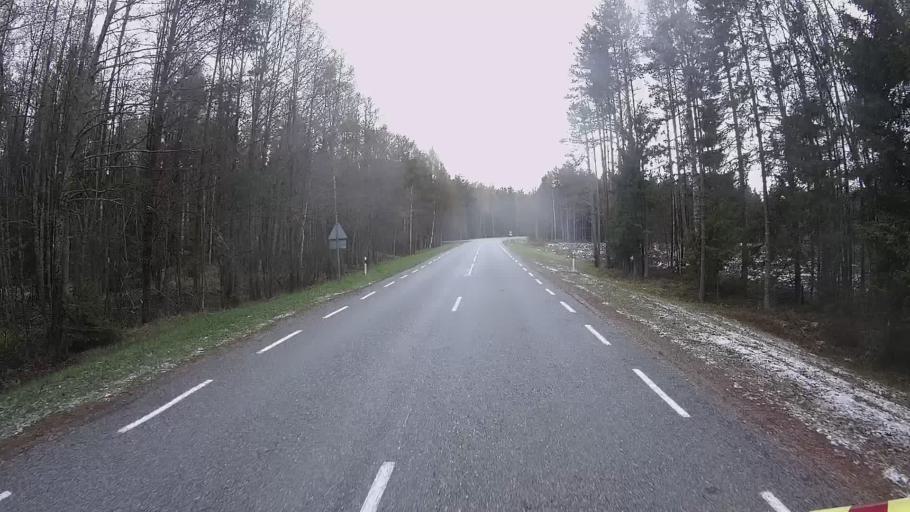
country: EE
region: Hiiumaa
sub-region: Kaerdla linn
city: Kardla
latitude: 59.0400
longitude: 22.6823
